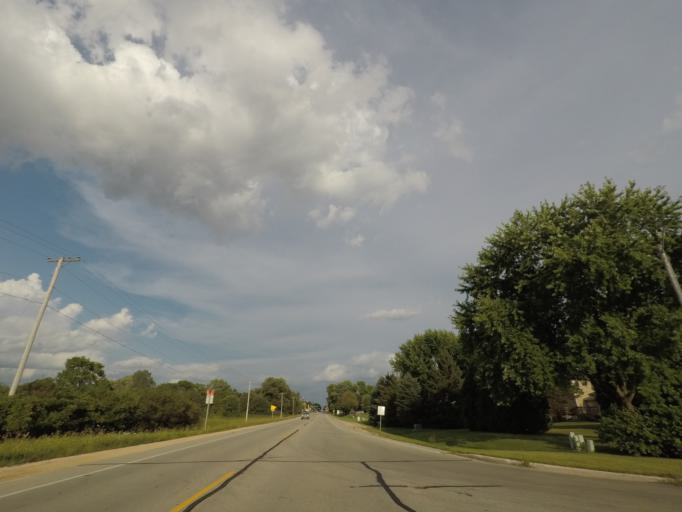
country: US
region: Wisconsin
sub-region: Dane County
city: Waunakee
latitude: 43.1921
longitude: -89.4707
